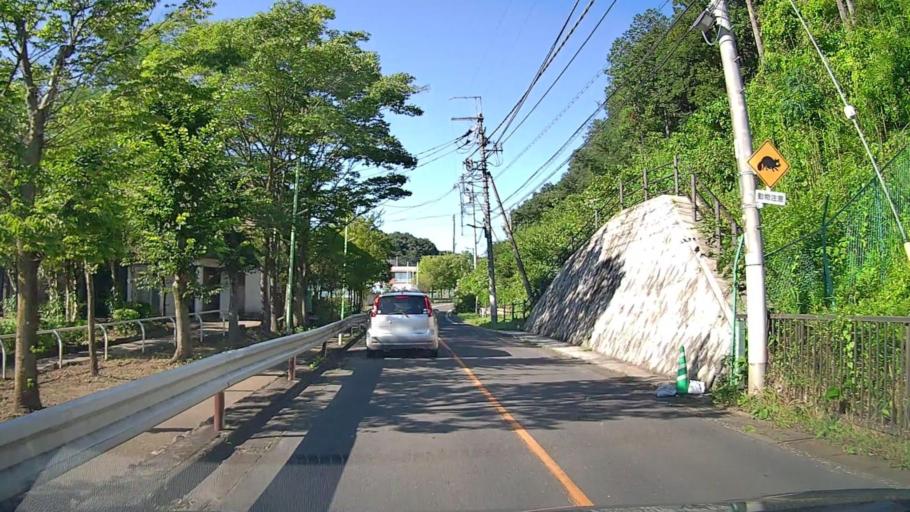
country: JP
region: Tokyo
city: Fussa
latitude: 35.7731
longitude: 139.3566
